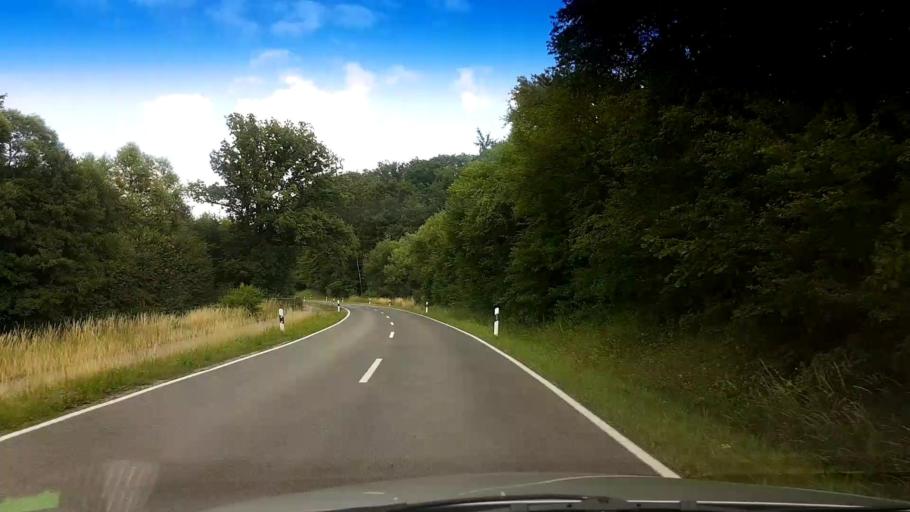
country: DE
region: Bavaria
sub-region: Upper Franconia
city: Gerach
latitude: 50.0022
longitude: 10.7989
